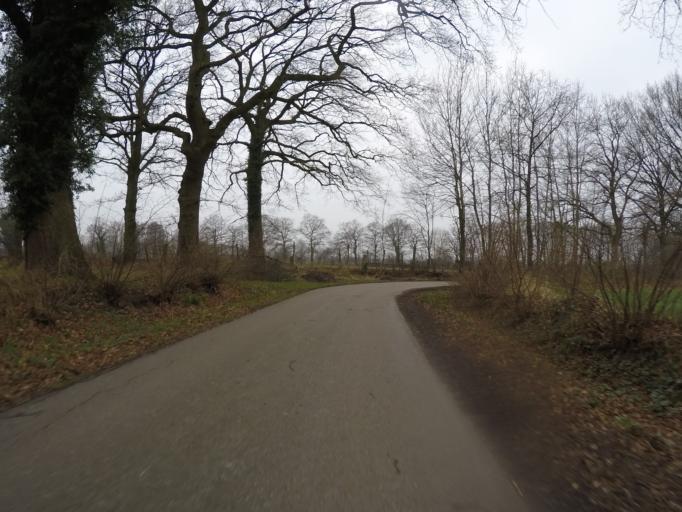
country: DE
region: Schleswig-Holstein
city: Tangstedt
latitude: 53.6832
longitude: 9.8426
